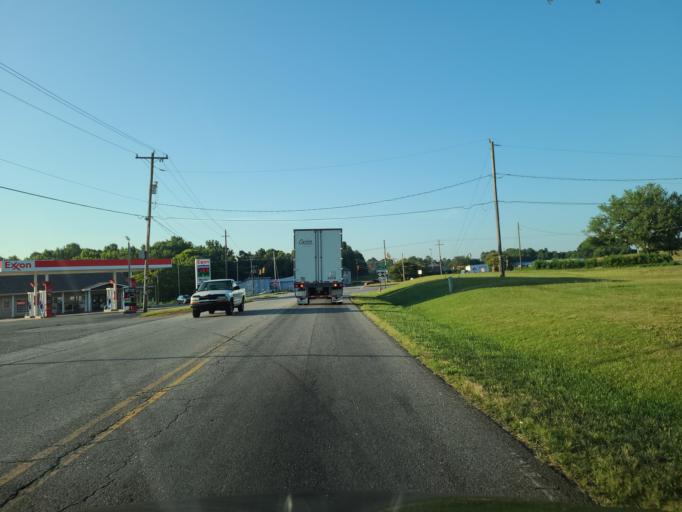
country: US
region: North Carolina
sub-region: Catawba County
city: Mountain View
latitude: 35.6278
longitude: -81.3761
